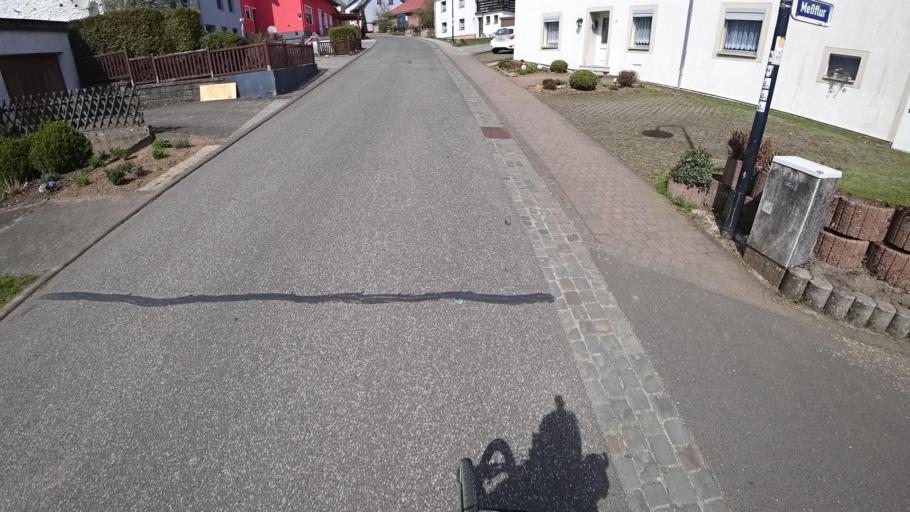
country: DE
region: Rheinland-Pfalz
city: Kell
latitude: 49.6368
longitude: 6.8211
